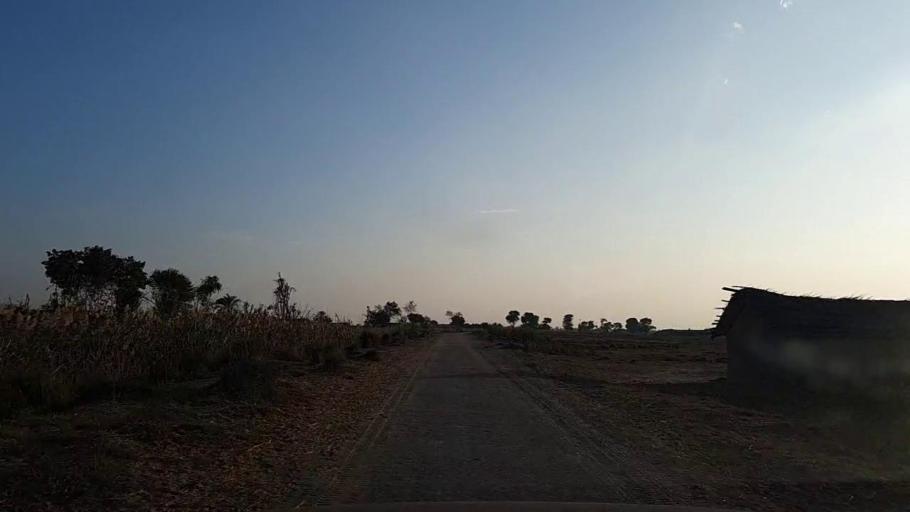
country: PK
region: Sindh
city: Sanghar
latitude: 26.2679
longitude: 68.9817
